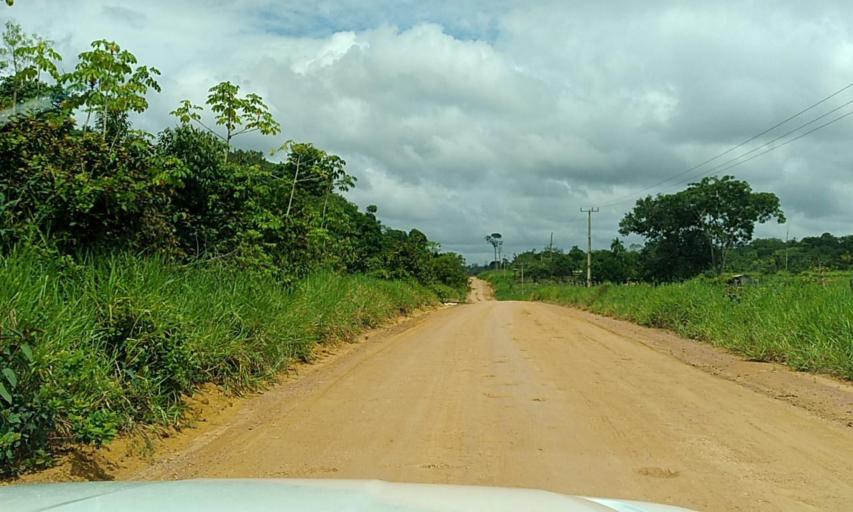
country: BR
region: Para
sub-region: Senador Jose Porfirio
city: Senador Jose Porfirio
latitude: -2.7760
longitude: -51.7774
